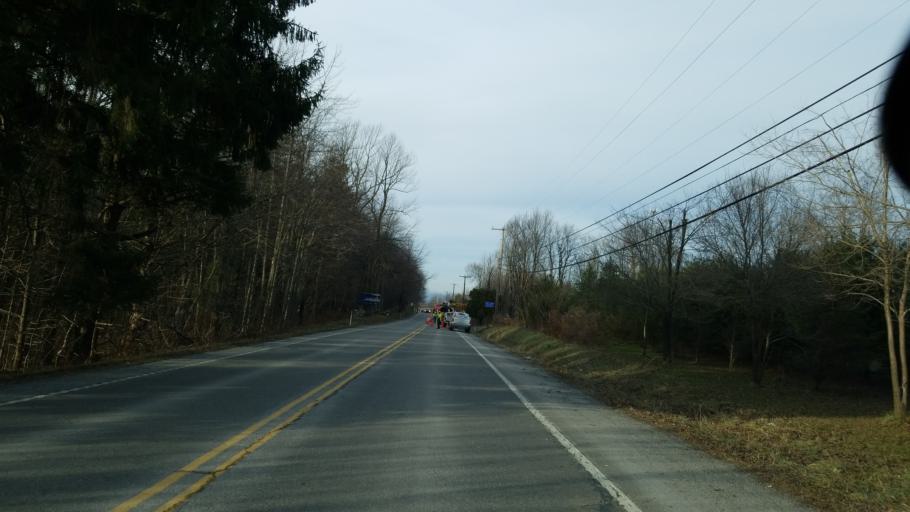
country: US
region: Pennsylvania
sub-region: Clearfield County
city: Sandy
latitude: 41.0463
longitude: -78.7025
